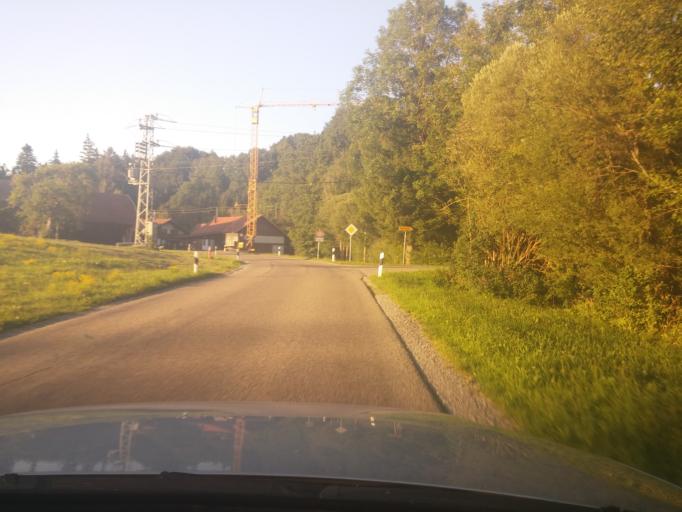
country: DE
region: Bavaria
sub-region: Swabia
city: Altusried
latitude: 47.8168
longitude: 10.1792
